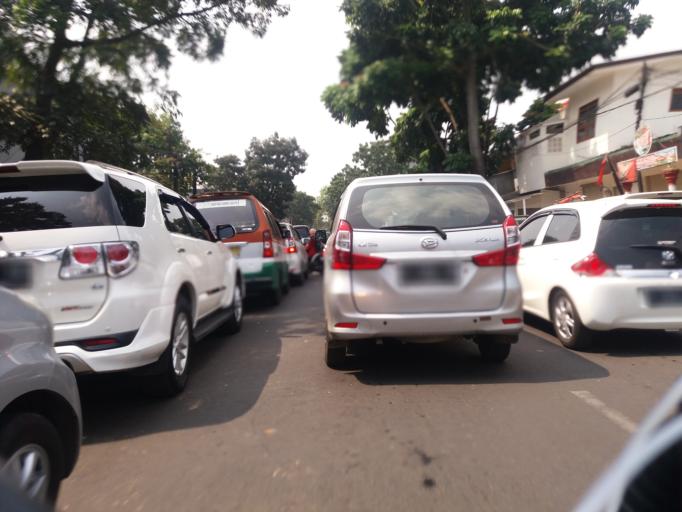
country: ID
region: West Java
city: Bandung
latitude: -6.9161
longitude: 107.5867
